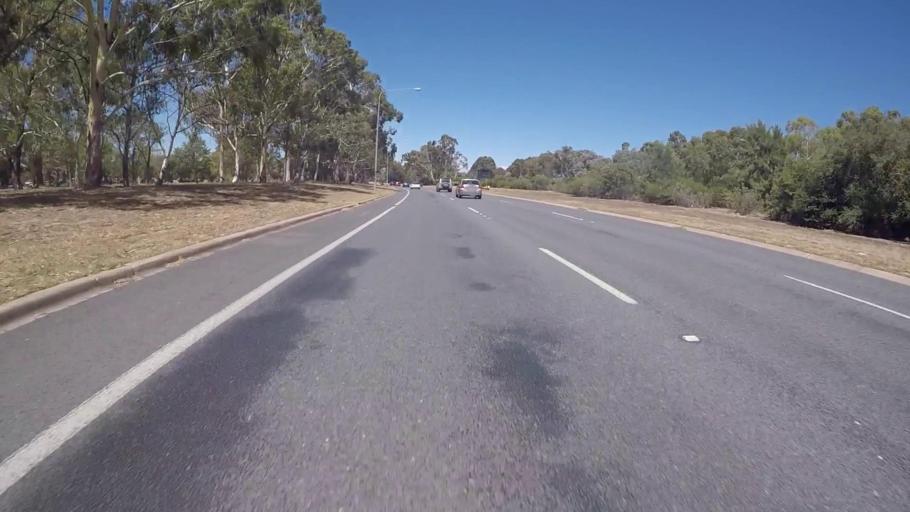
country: AU
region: Australian Capital Territory
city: Macarthur
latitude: -35.3824
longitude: 149.0577
